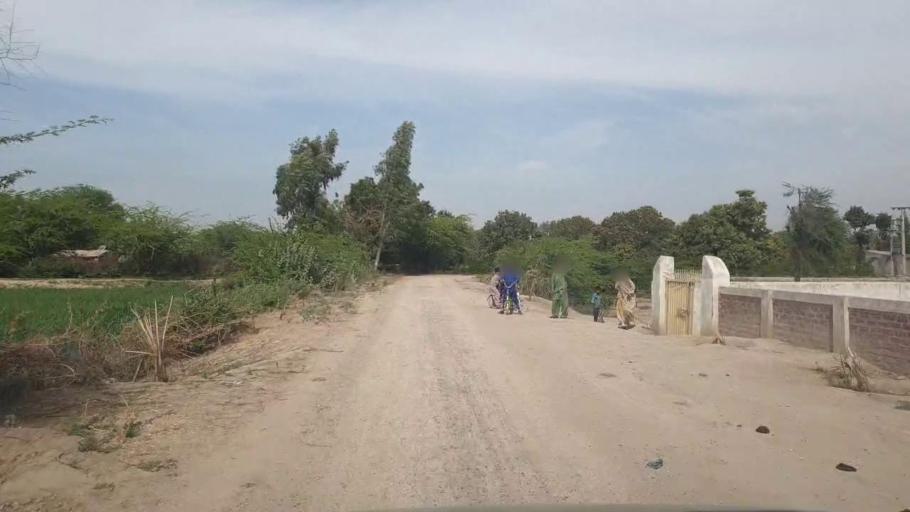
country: PK
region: Sindh
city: Kunri
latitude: 25.2037
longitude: 69.6915
